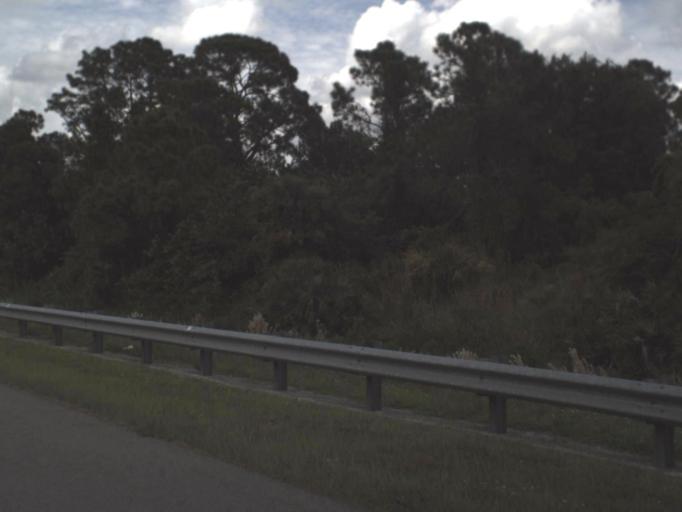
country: US
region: Florida
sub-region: Collier County
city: Immokalee
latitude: 26.4105
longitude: -81.3997
